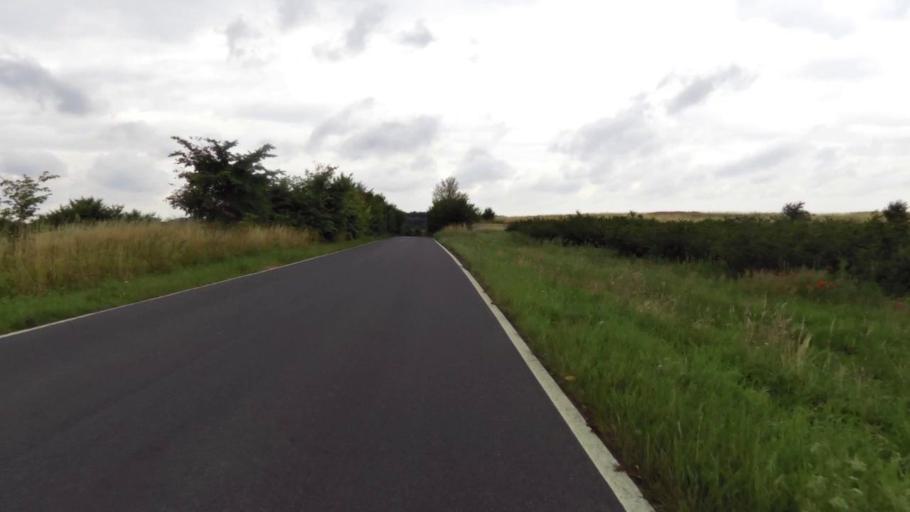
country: PL
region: West Pomeranian Voivodeship
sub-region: Powiat mysliborski
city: Mysliborz
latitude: 52.9384
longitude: 14.8755
